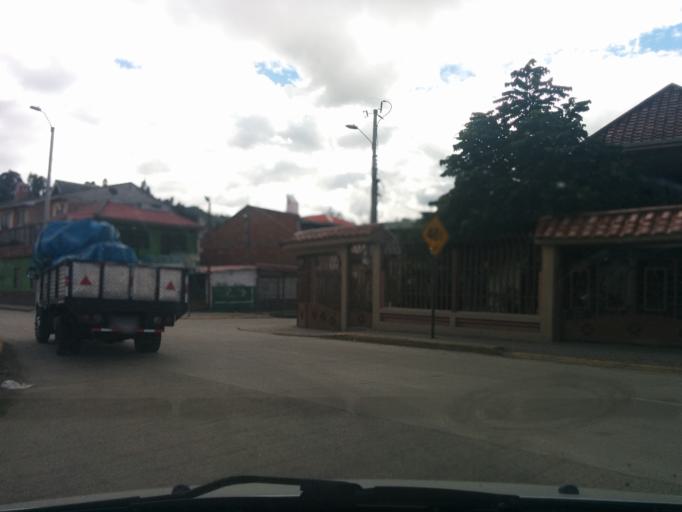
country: EC
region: Azuay
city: Cuenca
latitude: -2.9247
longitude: -79.0404
